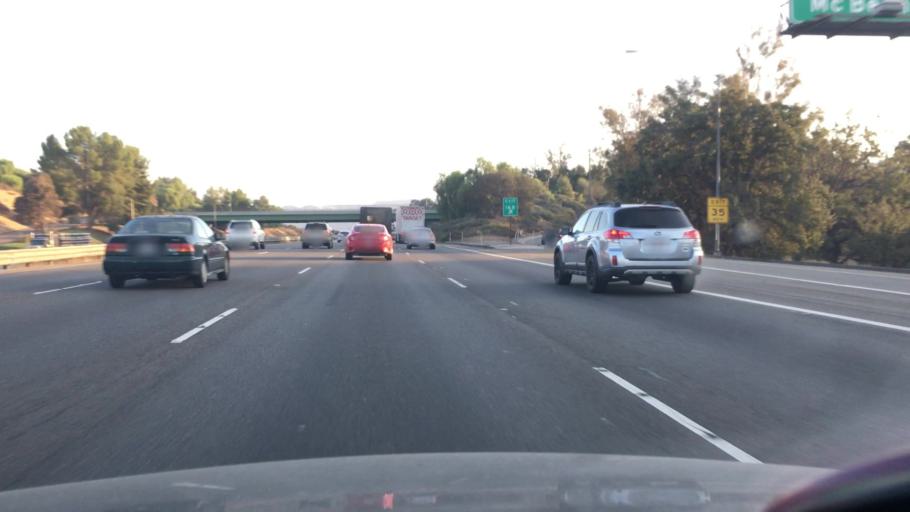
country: US
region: California
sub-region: Los Angeles County
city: Santa Clarita
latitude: 34.3970
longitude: -118.5721
